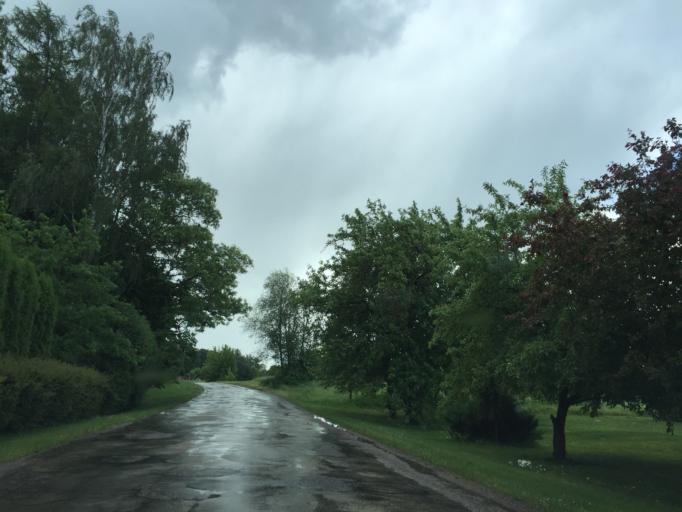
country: LV
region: Lecava
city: Iecava
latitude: 56.5959
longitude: 24.1884
